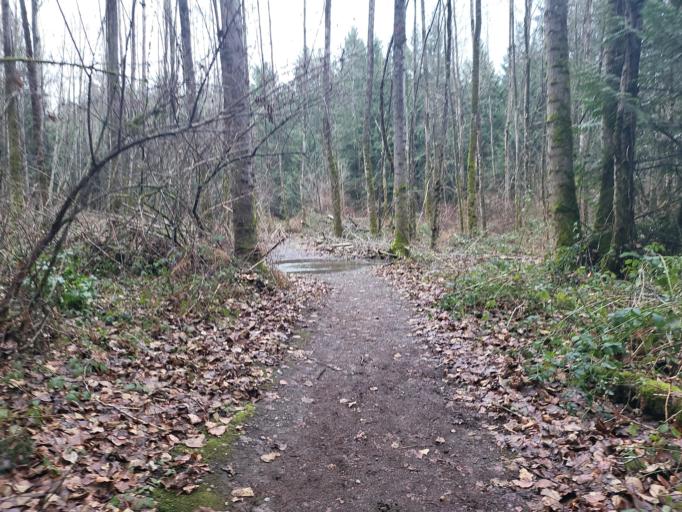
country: US
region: Washington
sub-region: King County
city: East Renton Highlands
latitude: 47.4804
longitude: -122.1424
